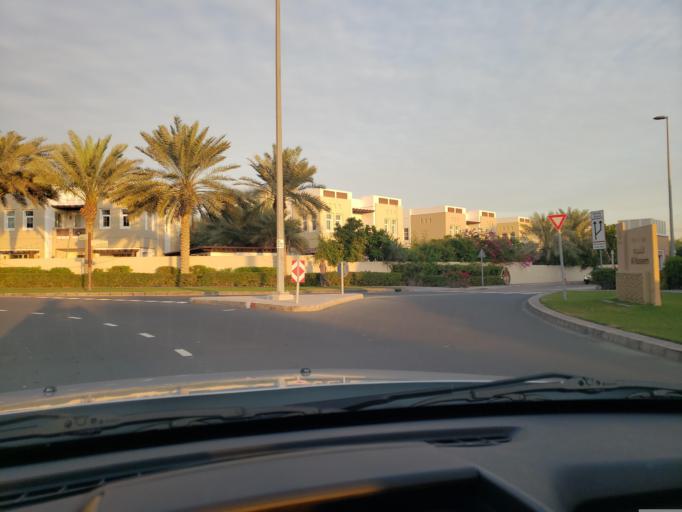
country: AE
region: Dubai
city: Dubai
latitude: 25.0201
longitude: 55.2738
